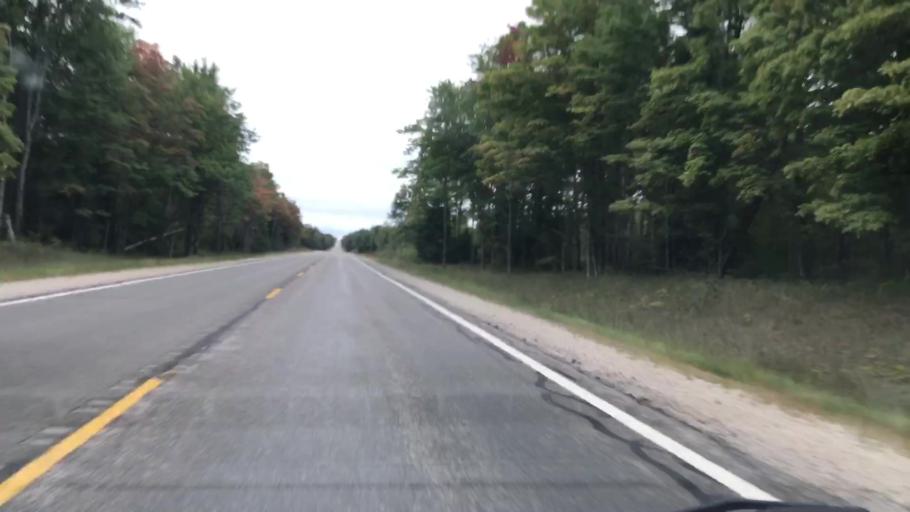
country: US
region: Michigan
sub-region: Luce County
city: Newberry
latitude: 46.2415
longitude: -85.5723
